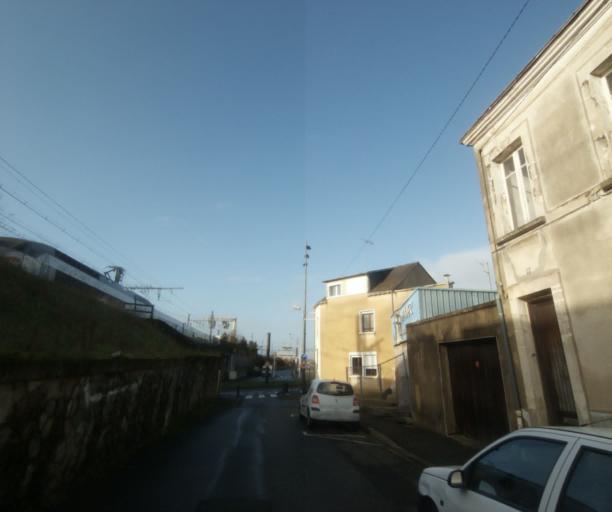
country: FR
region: Pays de la Loire
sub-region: Departement de la Sarthe
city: Le Mans
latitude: 47.9924
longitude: 0.2055
